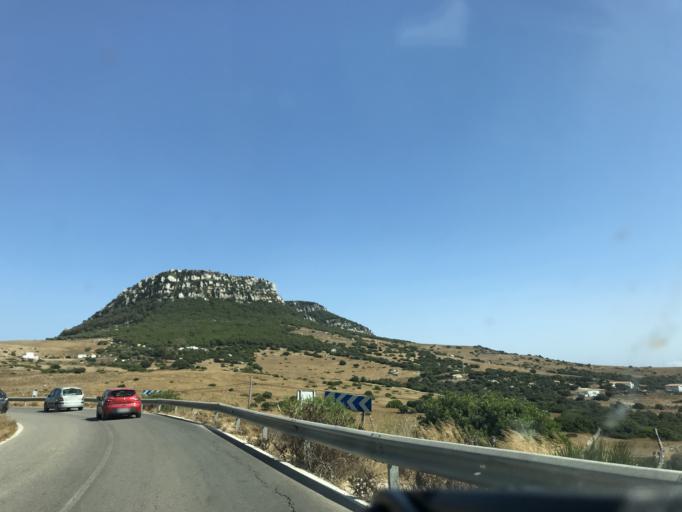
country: ES
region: Andalusia
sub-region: Provincia de Cadiz
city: Zahara de los Atunes
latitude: 36.1019
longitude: -5.7390
